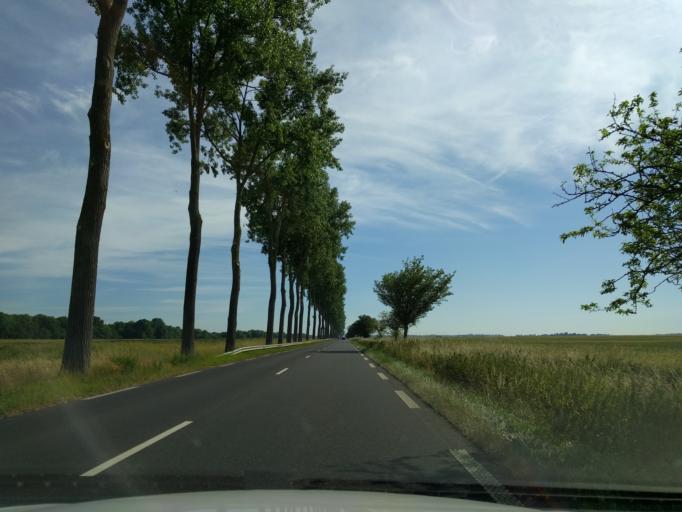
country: FR
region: Picardie
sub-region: Departement de l'Oise
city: Tille
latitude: 49.4726
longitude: 2.1241
